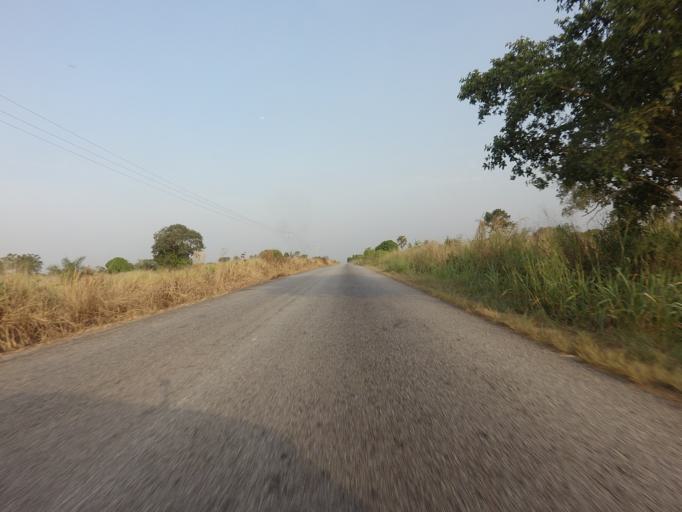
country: GH
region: Volta
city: Ho
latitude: 6.5735
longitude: 0.3544
